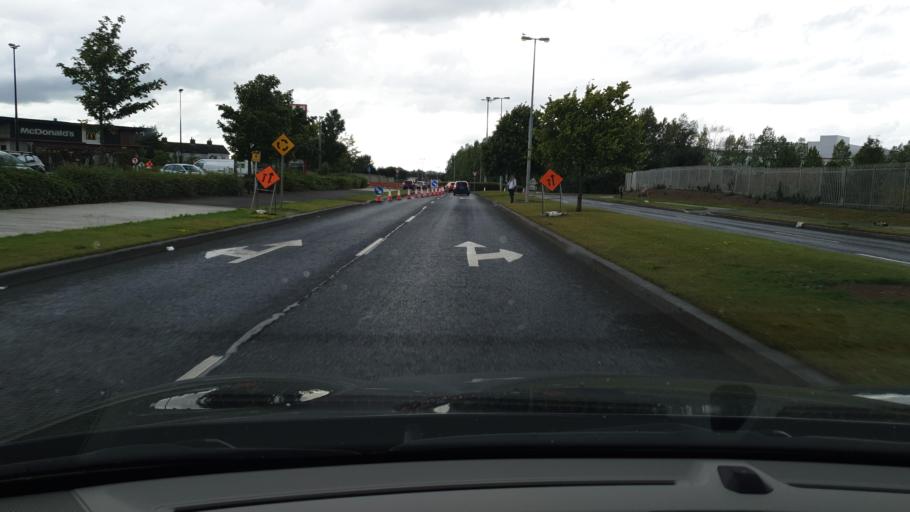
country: IE
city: Palmerstown
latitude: 53.3499
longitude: -6.3918
